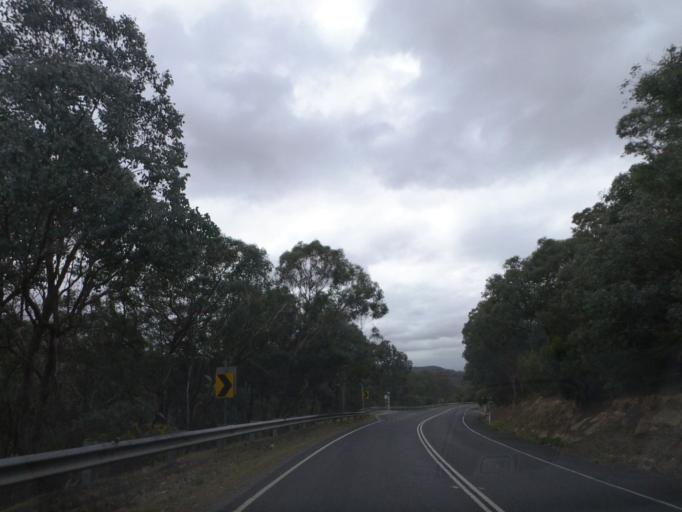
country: AU
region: Victoria
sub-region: Nillumbik
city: North Warrandyte
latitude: -37.7460
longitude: 145.2004
